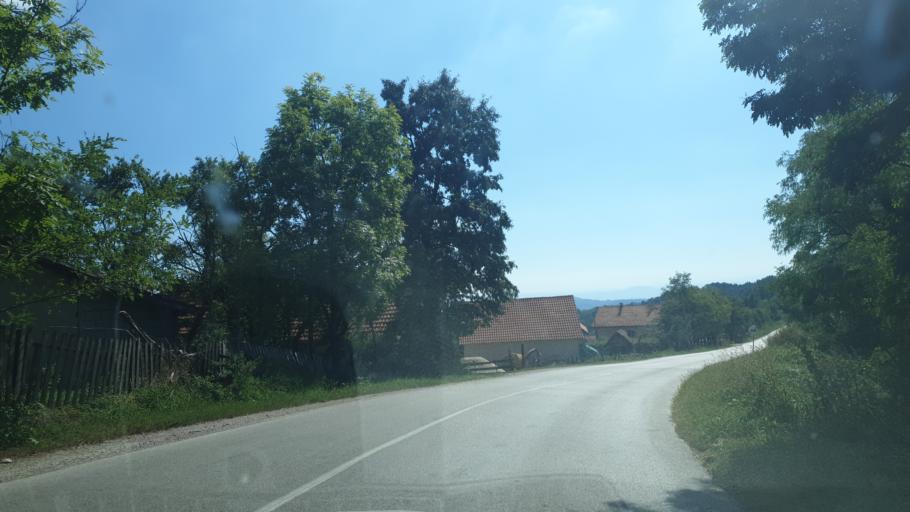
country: RS
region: Central Serbia
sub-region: Zlatiborski Okrug
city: Kosjeric
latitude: 43.9923
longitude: 20.0499
